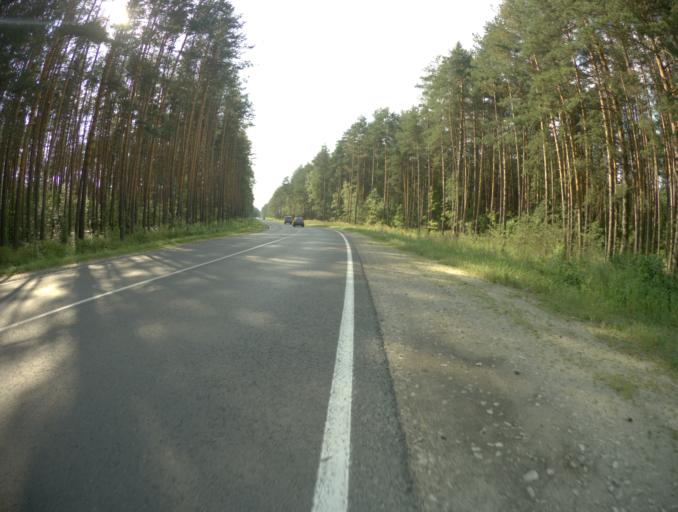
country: RU
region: Vladimir
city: Raduzhnyy
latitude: 56.0300
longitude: 40.3763
